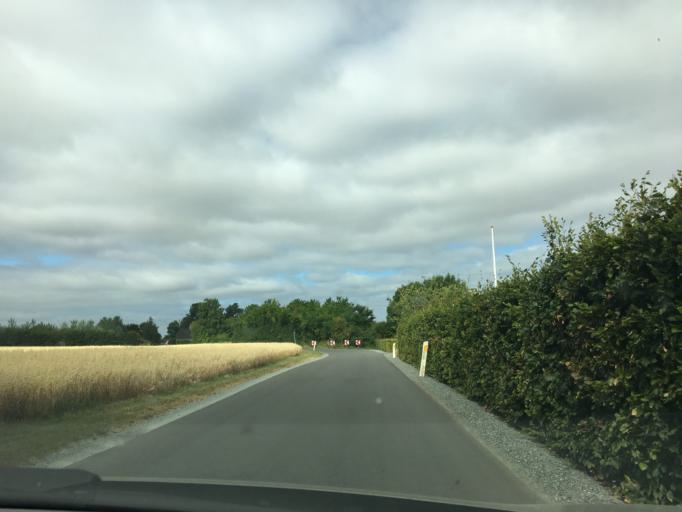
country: DK
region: South Denmark
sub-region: Middelfart Kommune
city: Norre Aby
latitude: 55.5069
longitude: 9.8613
